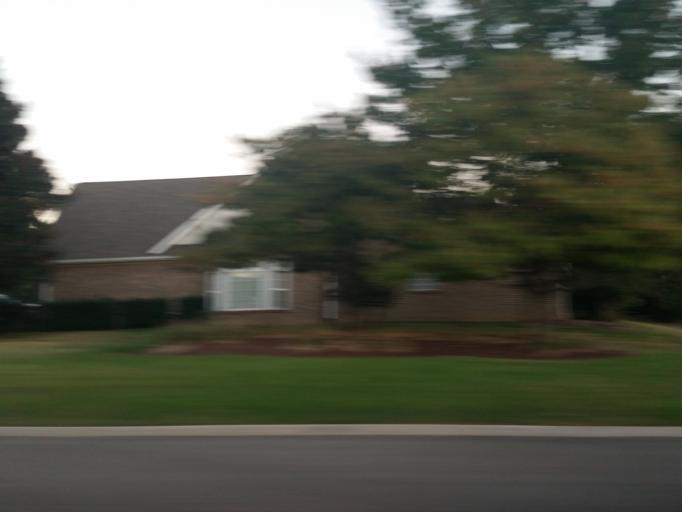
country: US
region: Tennessee
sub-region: Knox County
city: Knoxville
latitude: 36.0575
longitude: -83.8917
